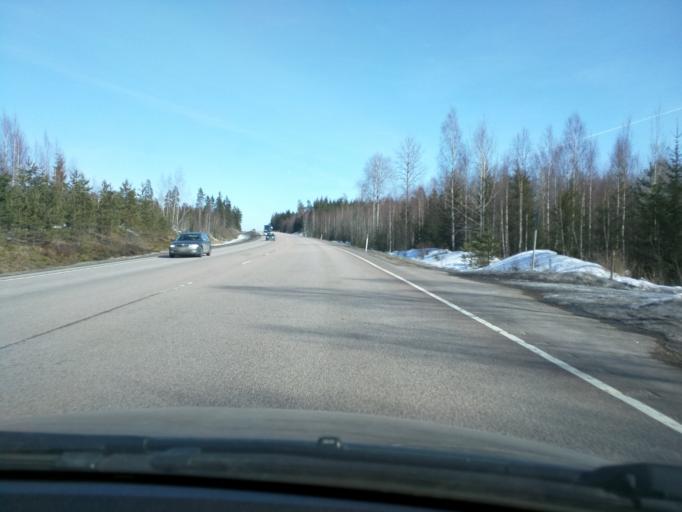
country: FI
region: Kymenlaakso
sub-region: Kouvola
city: Elimaeki
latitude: 60.7175
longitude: 26.3802
